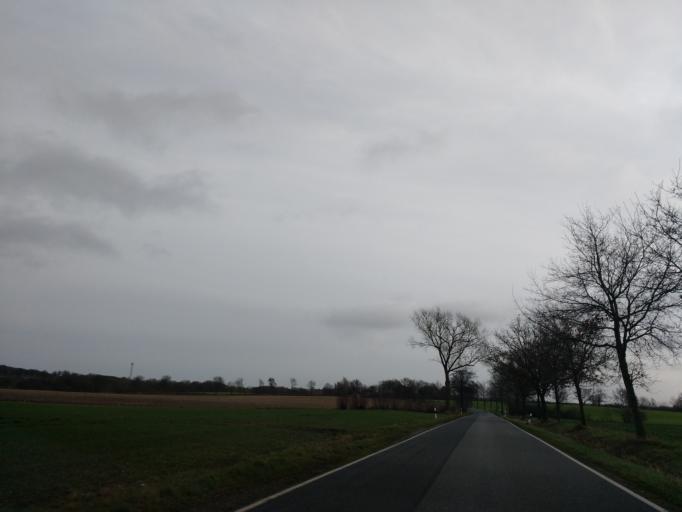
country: DE
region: Schleswig-Holstein
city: Susel
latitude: 54.0137
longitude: 10.6640
